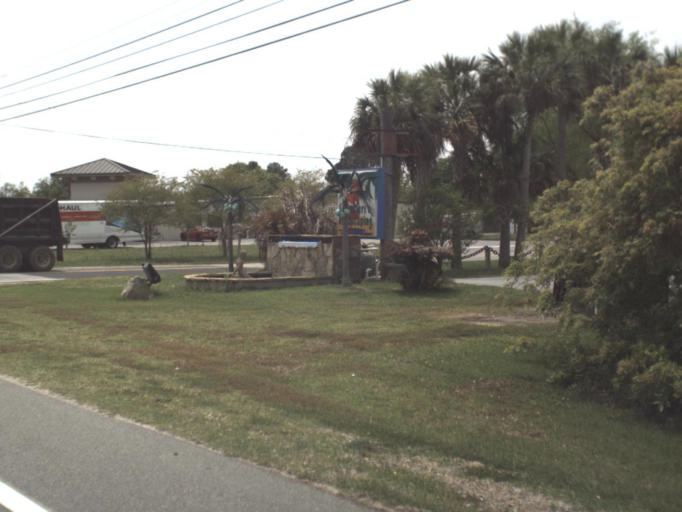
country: US
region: Florida
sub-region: Escambia County
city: Bellview
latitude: 30.4693
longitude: -87.3240
